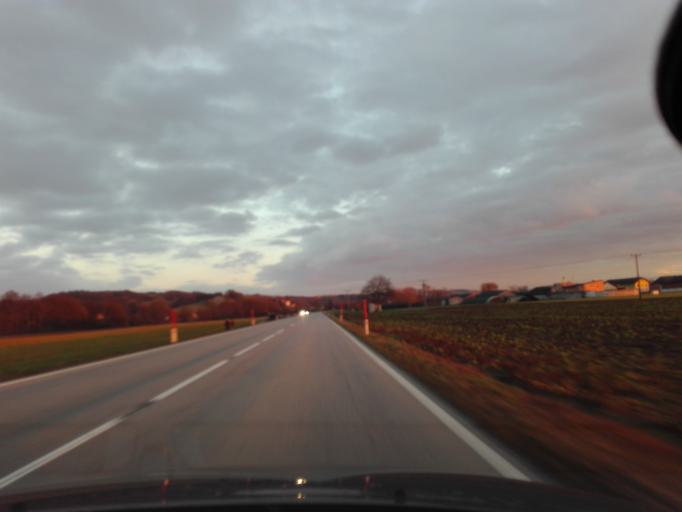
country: AT
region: Upper Austria
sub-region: Politischer Bezirk Perg
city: Bad Kreuzen
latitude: 48.2112
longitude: 14.7734
